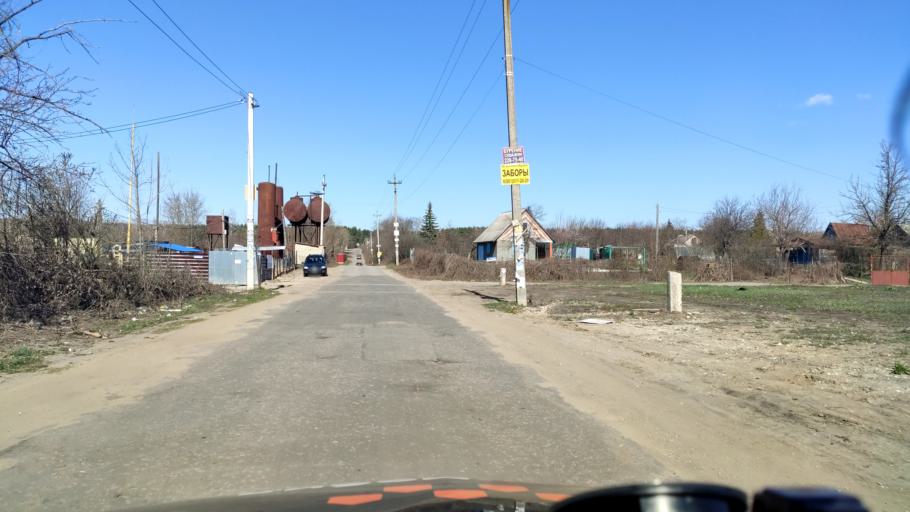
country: RU
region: Voronezj
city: Shilovo
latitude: 51.6006
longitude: 39.1430
